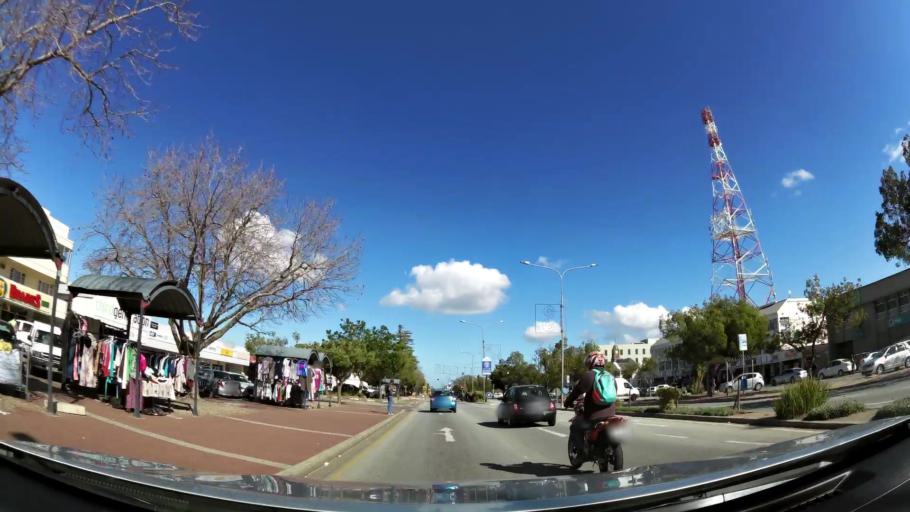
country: ZA
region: Western Cape
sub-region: Eden District Municipality
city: George
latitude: -33.9593
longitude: 22.4564
